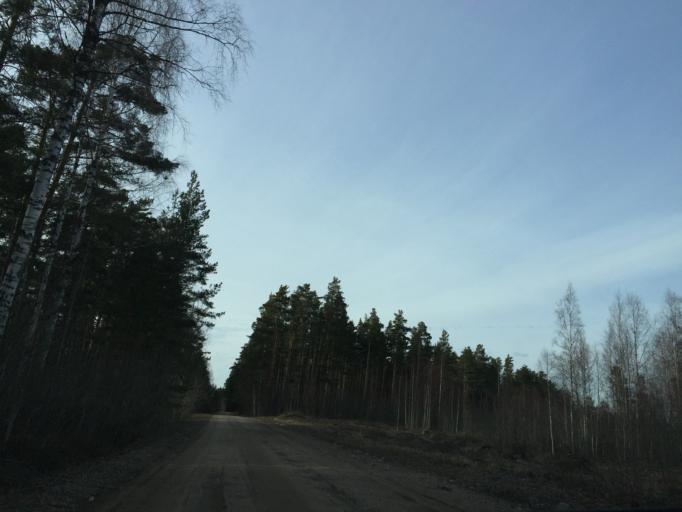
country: EE
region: Paernumaa
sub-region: Paernu linn
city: Parnu
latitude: 58.2139
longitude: 24.4975
